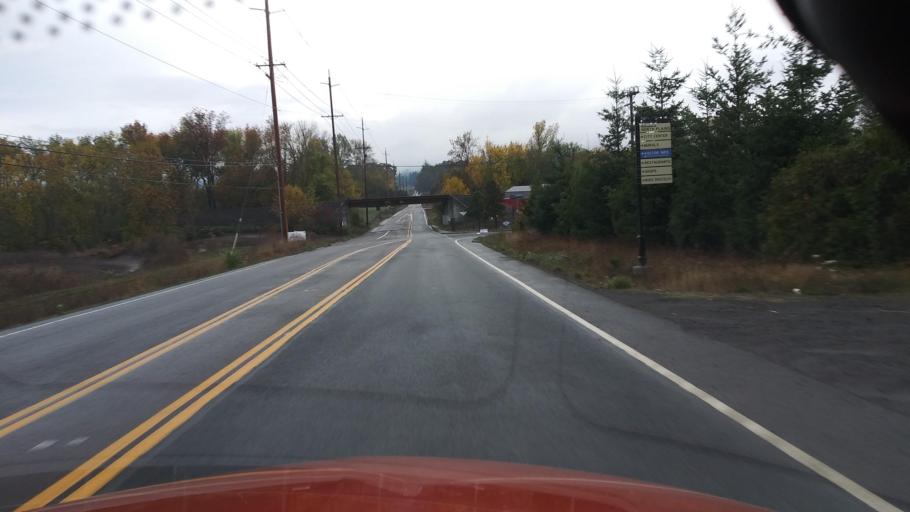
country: US
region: Oregon
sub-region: Washington County
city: North Plains
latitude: 45.5983
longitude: -123.0133
